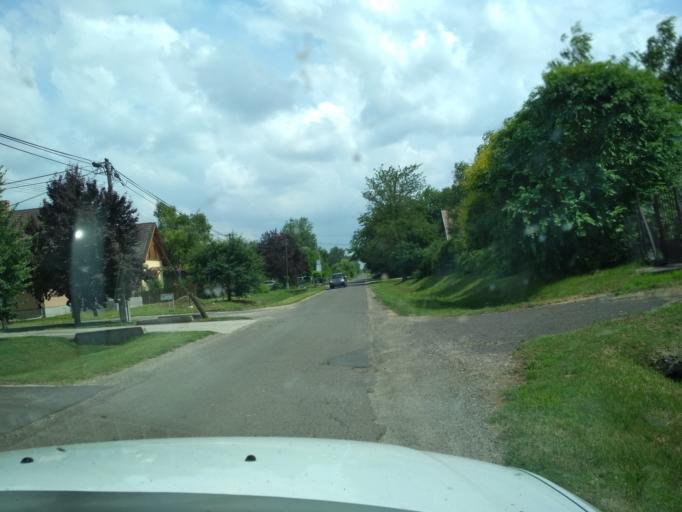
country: HU
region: Pest
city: Tapioszentmarton
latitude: 47.3285
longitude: 19.7602
